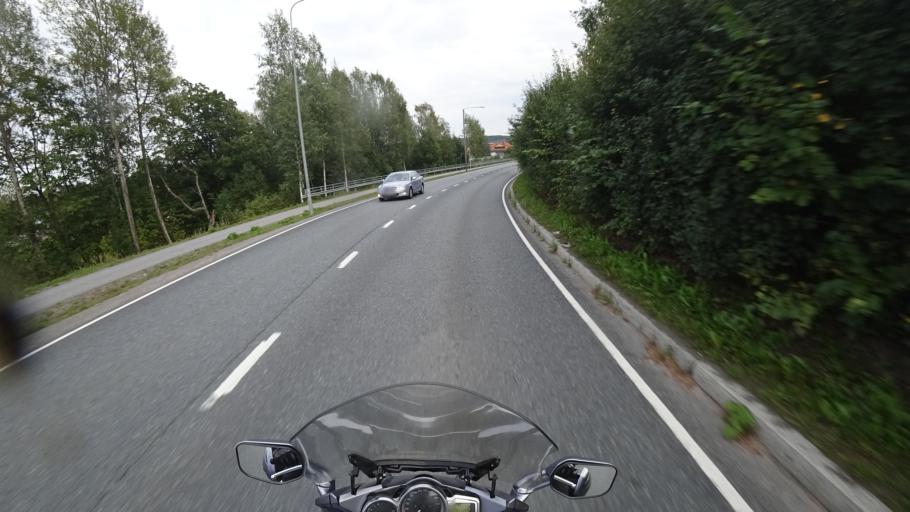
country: FI
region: Uusimaa
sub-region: Raaseporin
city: Karis
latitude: 60.0575
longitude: 23.6439
